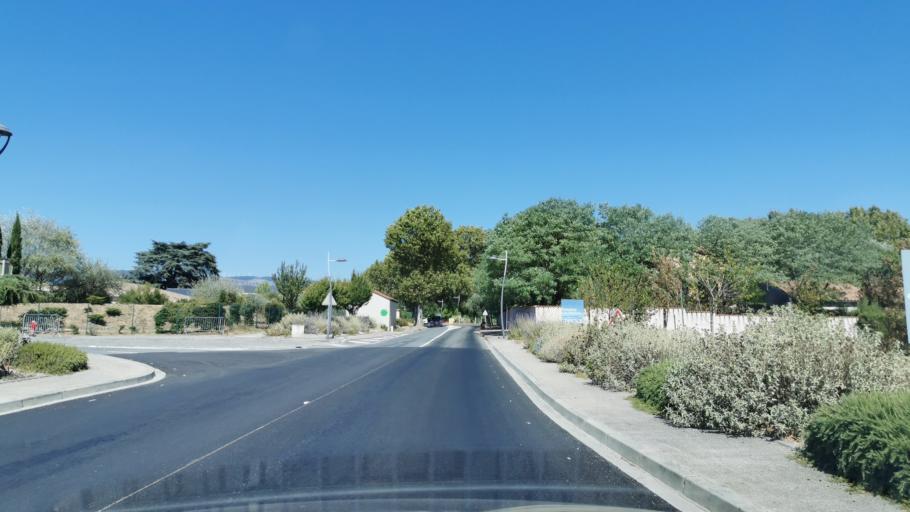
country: FR
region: Languedoc-Roussillon
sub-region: Departement de l'Aude
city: Conques-sur-Orbiel
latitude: 43.2822
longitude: 2.4374
